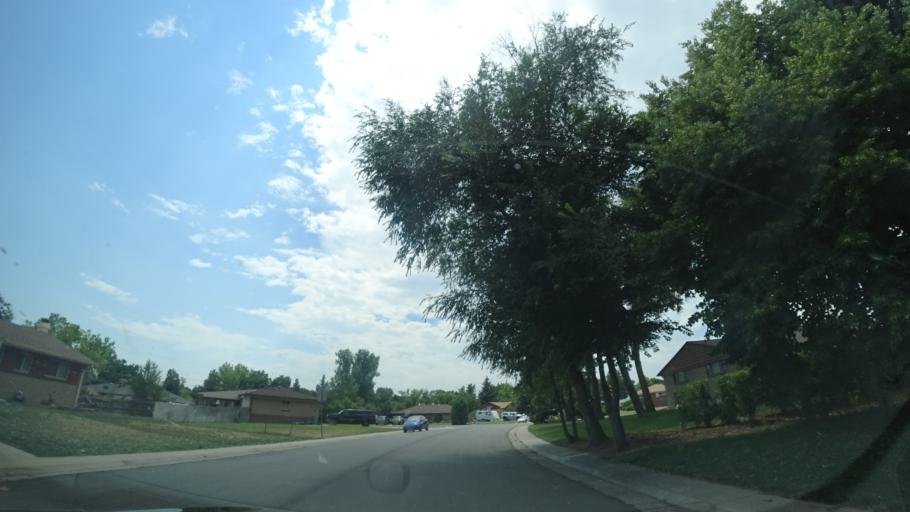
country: US
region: Colorado
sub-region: Jefferson County
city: Lakewood
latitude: 39.7245
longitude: -105.0969
